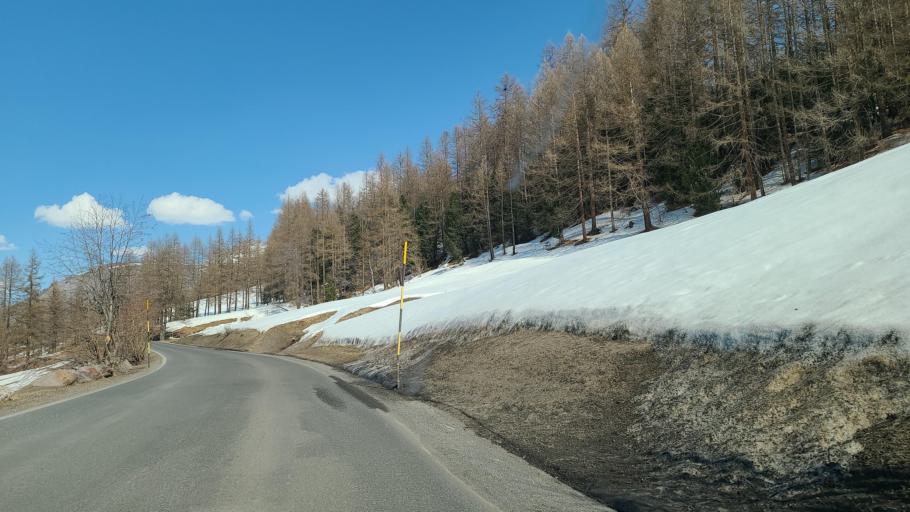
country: IT
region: Lombardy
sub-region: Provincia di Sondrio
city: Livigno
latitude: 46.5231
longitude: 10.1313
